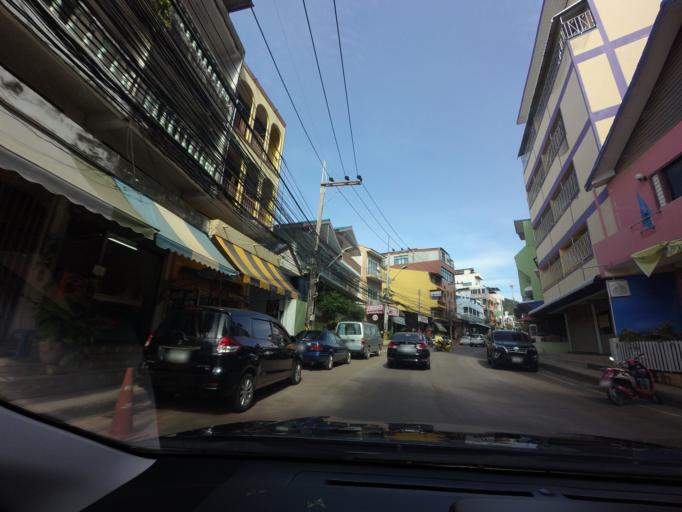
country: TH
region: Chon Buri
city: Si Racha
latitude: 13.1605
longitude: 100.9199
